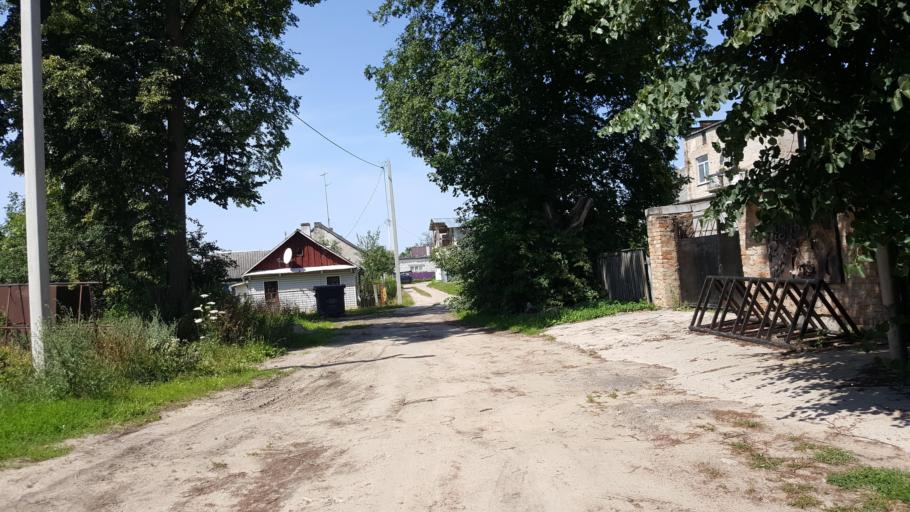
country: BY
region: Brest
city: Vysokaye
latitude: 52.3665
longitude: 23.3758
